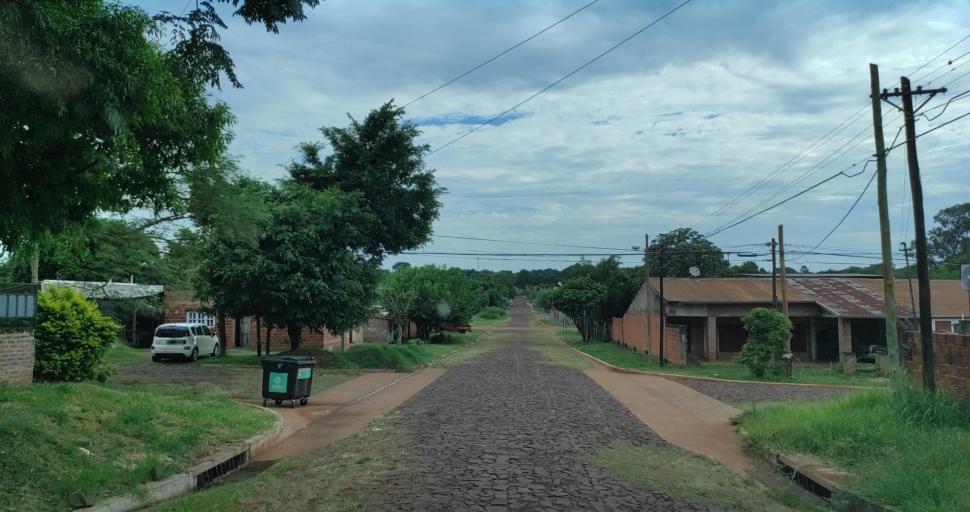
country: AR
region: Misiones
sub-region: Departamento de Capital
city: Posadas
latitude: -27.3926
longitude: -55.9305
